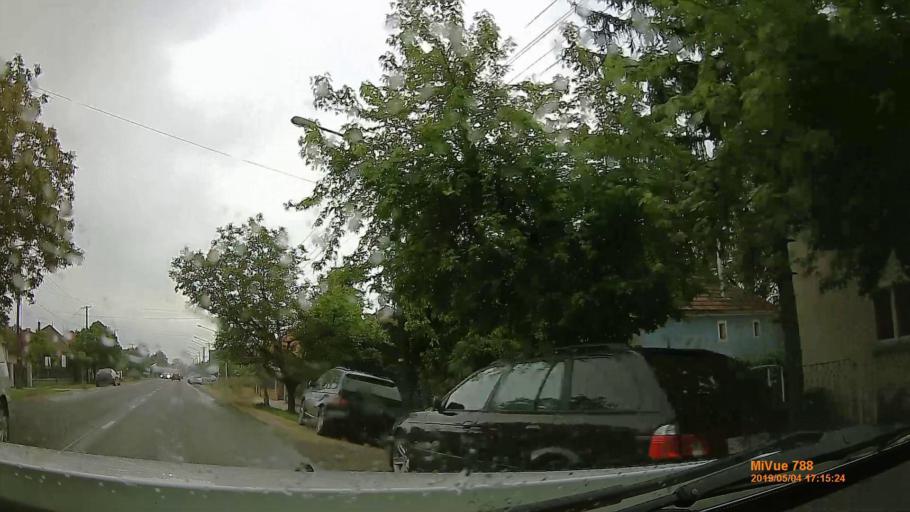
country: HU
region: Gyor-Moson-Sopron
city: Mosonmagyarovar
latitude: 47.8593
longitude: 17.2663
